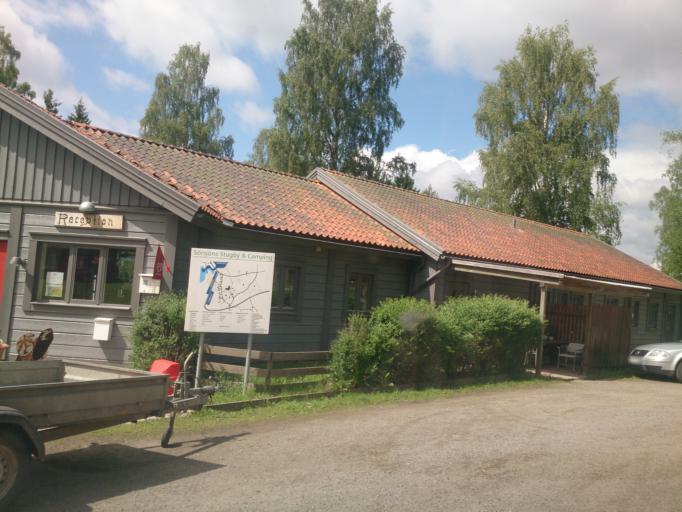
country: SE
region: OEstergoetland
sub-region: Norrkopings Kommun
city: Svartinge
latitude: 58.7217
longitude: 16.0857
